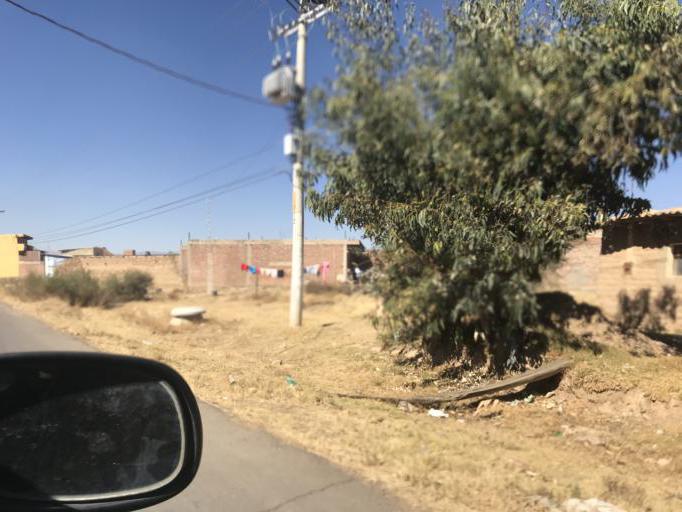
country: BO
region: Cochabamba
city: Cliza
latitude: -17.5987
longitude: -65.9603
